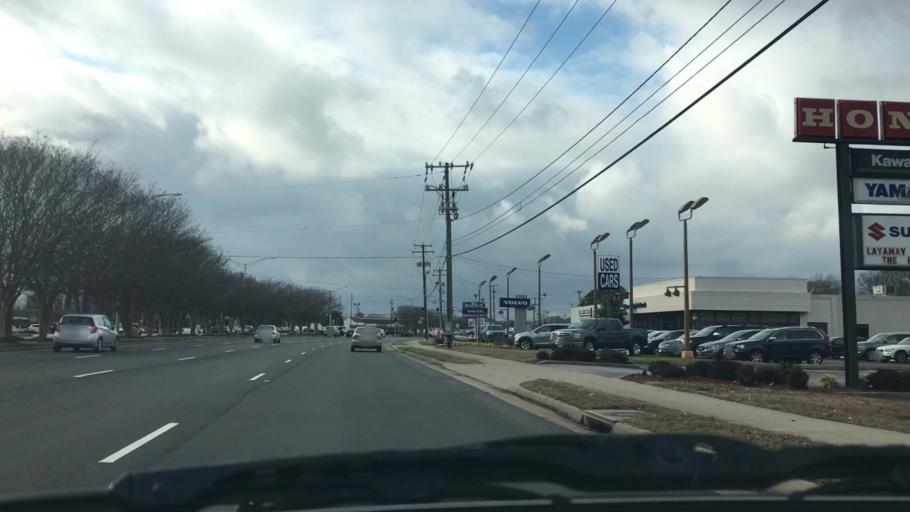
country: US
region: Virginia
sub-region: City of Chesapeake
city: Chesapeake
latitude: 36.8439
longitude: -76.1498
